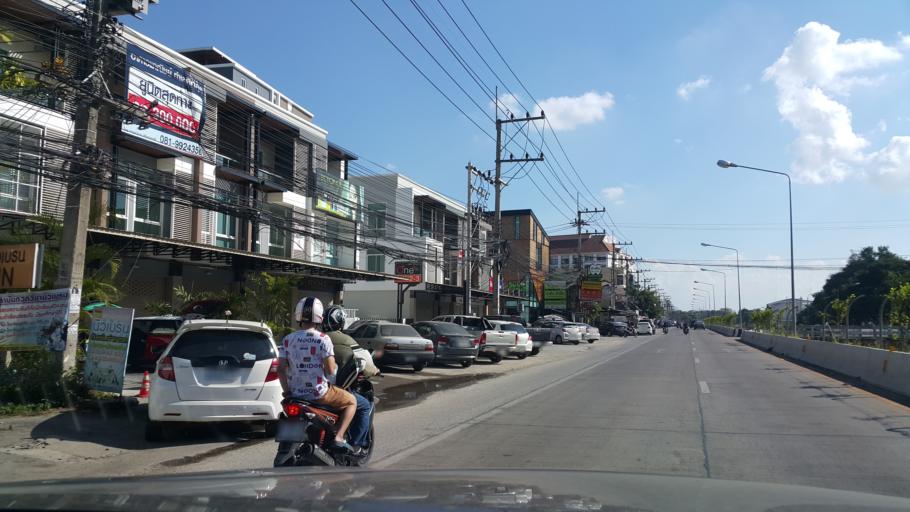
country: TH
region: Chiang Mai
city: Chiang Mai
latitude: 18.8010
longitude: 98.9603
